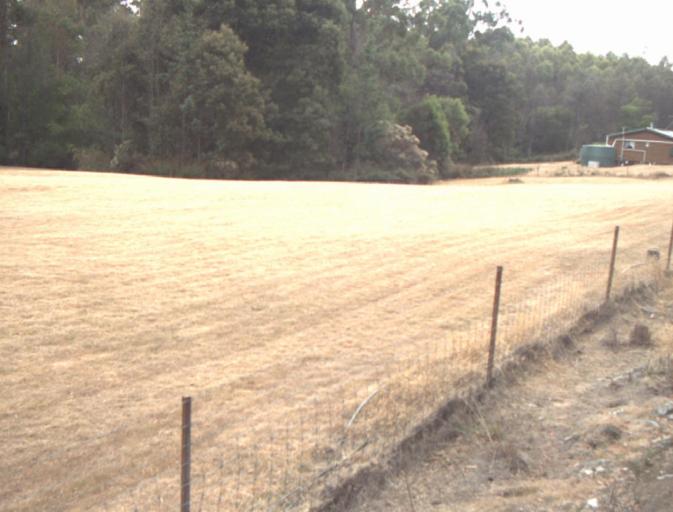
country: AU
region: Tasmania
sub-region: Launceston
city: Mayfield
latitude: -41.1983
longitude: 147.2315
